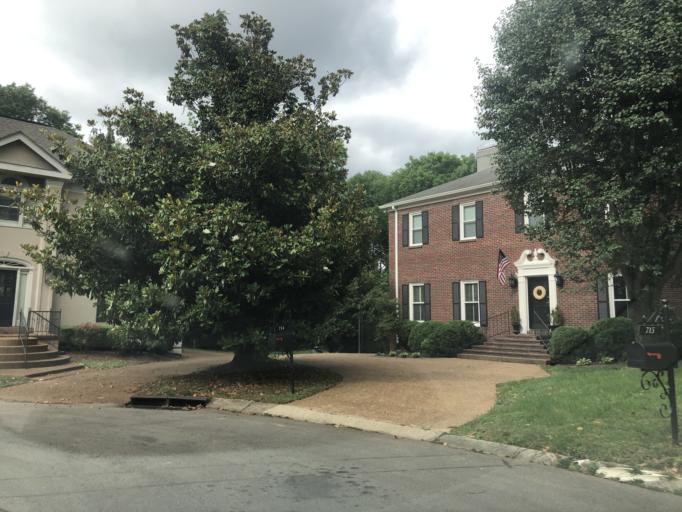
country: US
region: Tennessee
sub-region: Davidson County
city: Oak Hill
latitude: 36.0954
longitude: -86.8130
